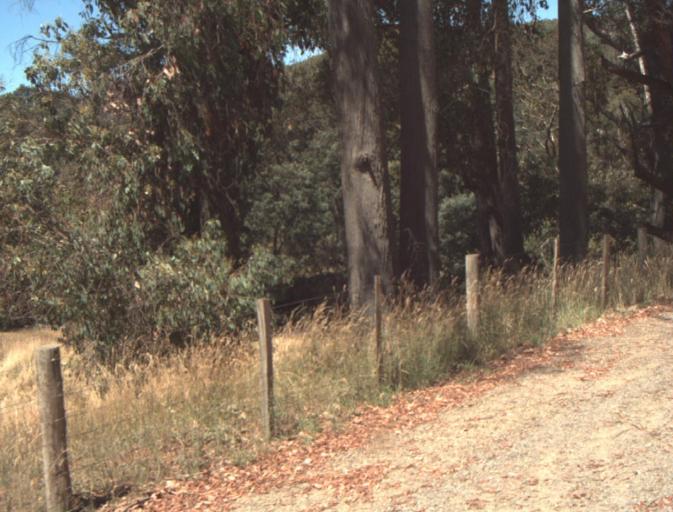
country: AU
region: Tasmania
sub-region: Dorset
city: Scottsdale
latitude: -41.2910
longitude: 147.3927
